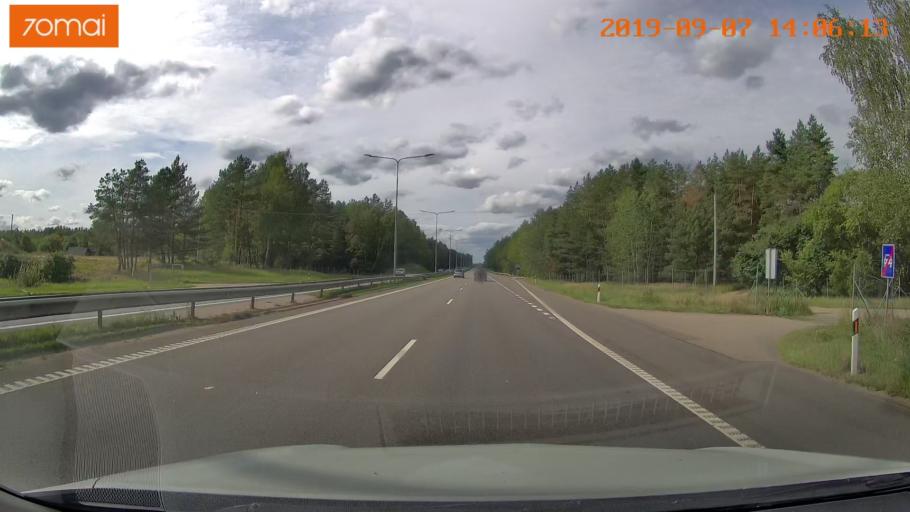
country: LT
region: Vilnius County
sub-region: Vilniaus Rajonas
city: Vievis
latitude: 54.7573
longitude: 24.8892
